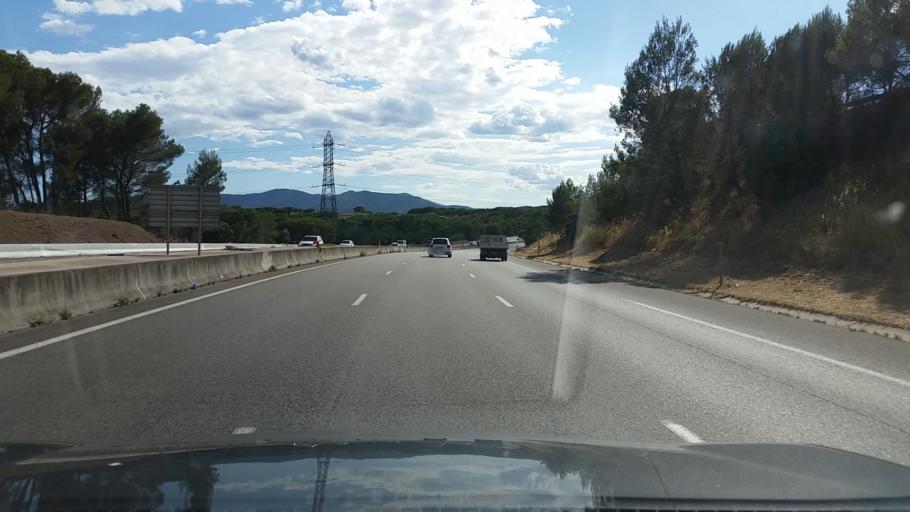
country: FR
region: Provence-Alpes-Cote d'Azur
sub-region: Departement du Var
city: Puget-sur-Argens
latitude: 43.4588
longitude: 6.7080
